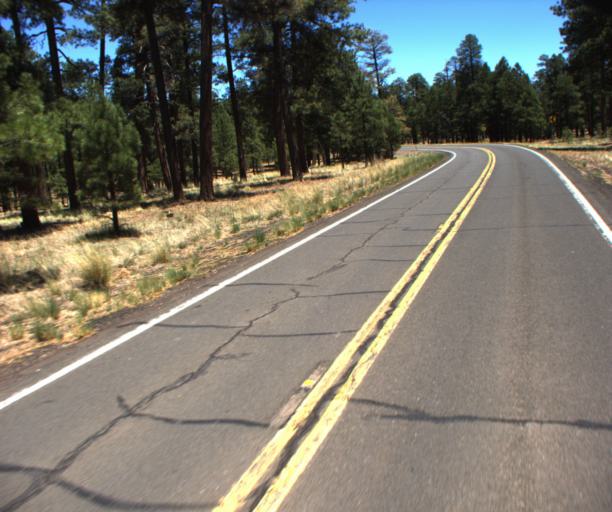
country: US
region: Arizona
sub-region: Gila County
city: Pine
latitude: 34.6077
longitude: -111.1950
